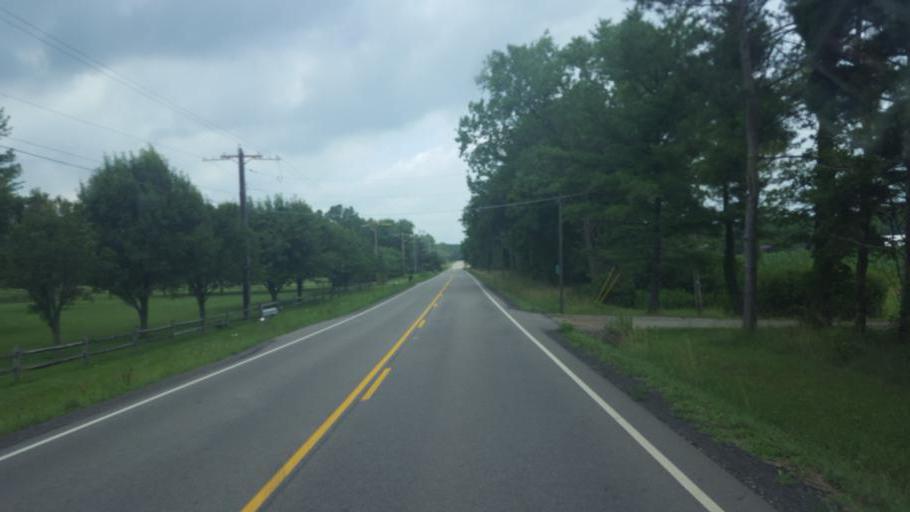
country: US
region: Ohio
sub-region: Licking County
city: Utica
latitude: 40.1719
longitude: -82.5191
